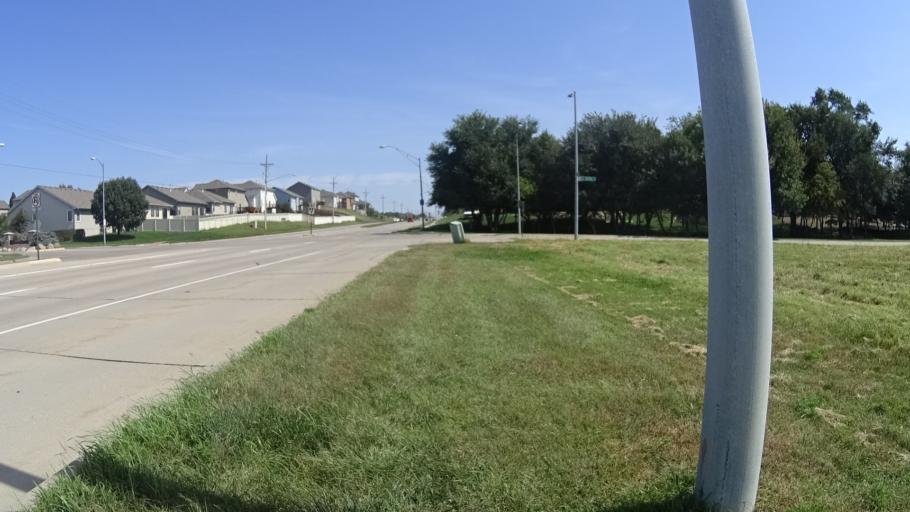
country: US
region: Nebraska
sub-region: Sarpy County
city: Papillion
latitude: 41.1761
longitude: -96.0780
